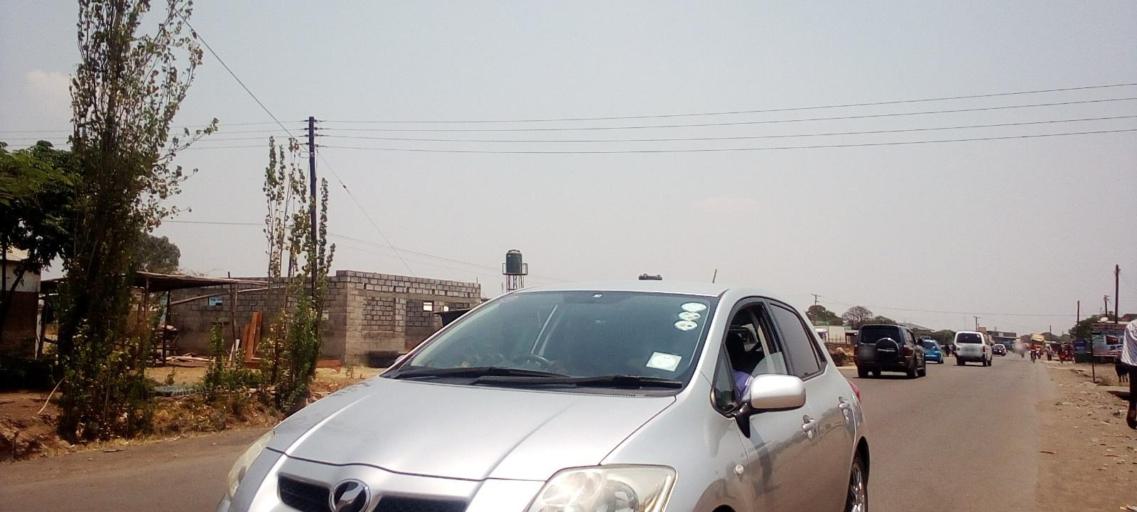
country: ZM
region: Lusaka
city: Lusaka
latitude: -15.4446
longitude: 28.2480
